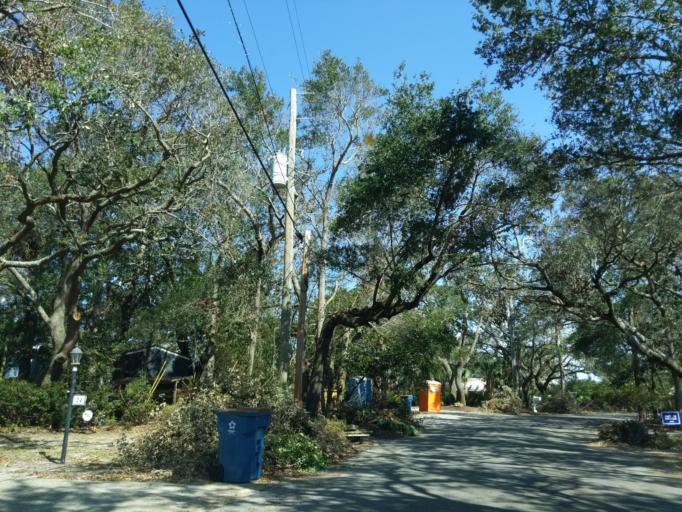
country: US
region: Florida
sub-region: Santa Rosa County
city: Gulf Breeze
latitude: 30.3638
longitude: -87.1819
